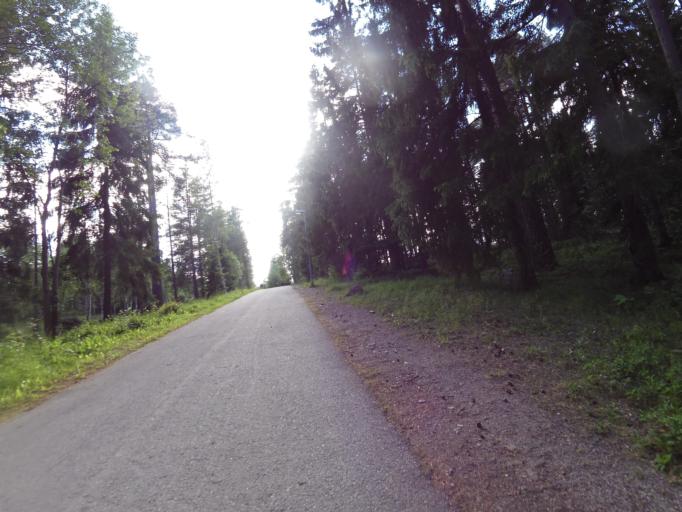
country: SE
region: Gaevleborg
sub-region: Gavle Kommun
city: Gavle
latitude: 60.6846
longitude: 17.1060
